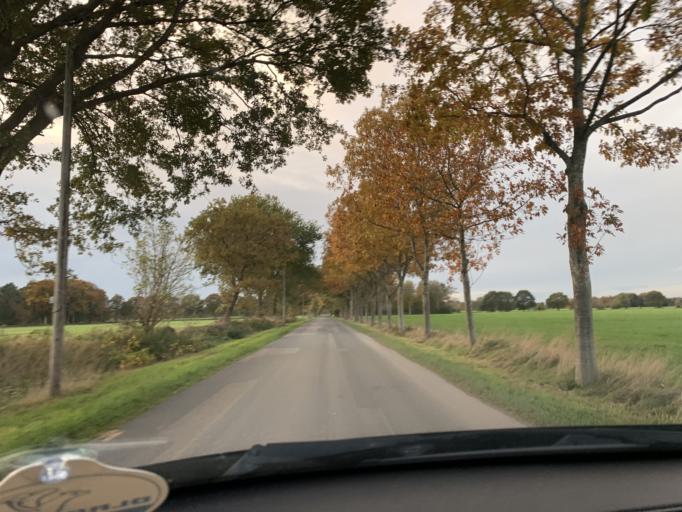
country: DE
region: Lower Saxony
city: Wiefelstede
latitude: 53.2628
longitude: 8.0964
